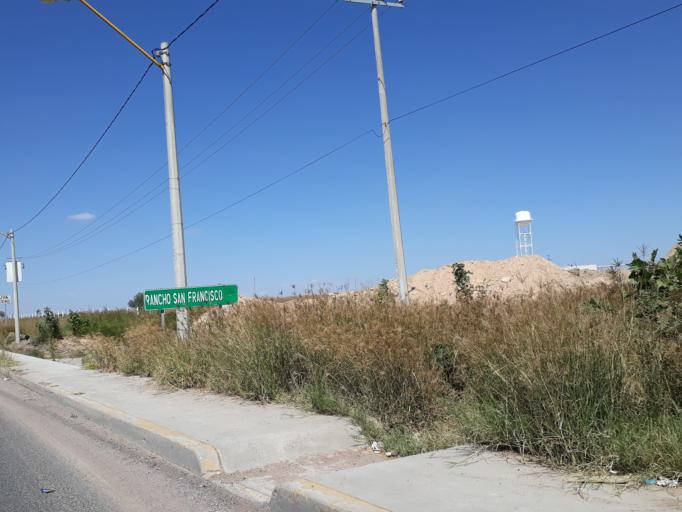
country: MX
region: Aguascalientes
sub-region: Aguascalientes
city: San Sebastian [Fraccionamiento]
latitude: 21.8101
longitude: -102.2919
